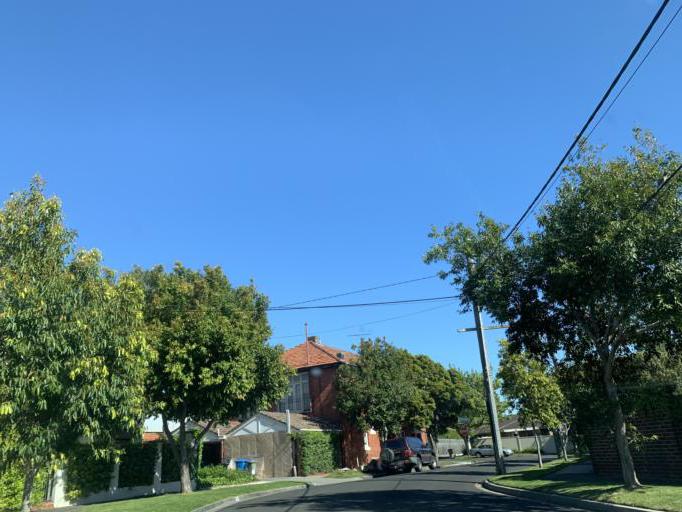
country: AU
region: Victoria
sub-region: Bayside
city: Hampton
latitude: -37.9251
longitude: 144.9999
